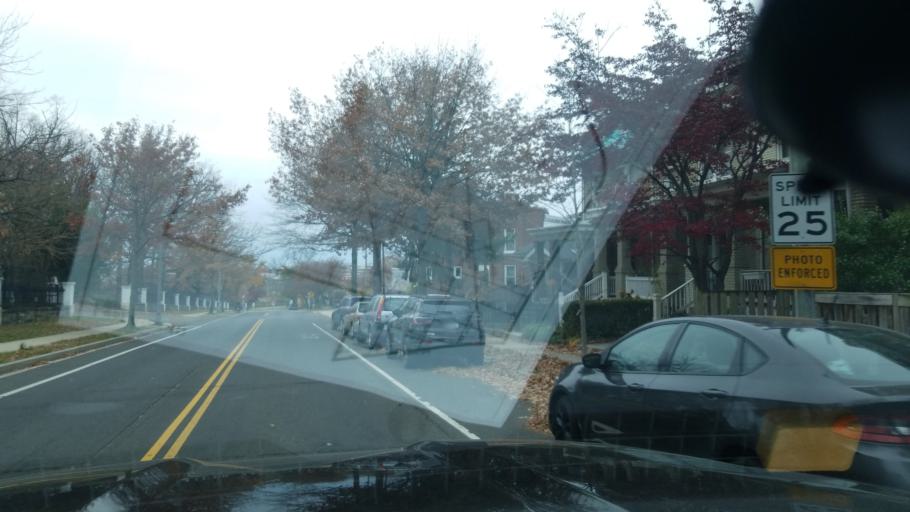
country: US
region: Maryland
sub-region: Prince George's County
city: Chillum
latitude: 38.9396
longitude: -77.0160
